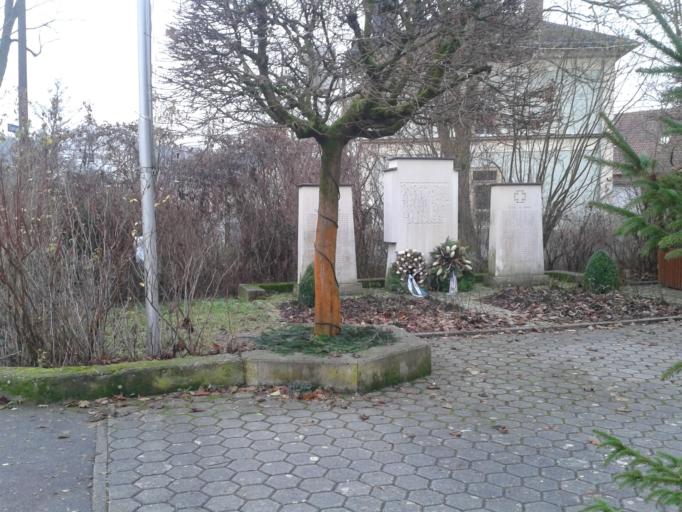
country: DE
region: Bavaria
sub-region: Upper Franconia
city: Memmelsdorf
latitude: 49.9422
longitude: 10.9716
